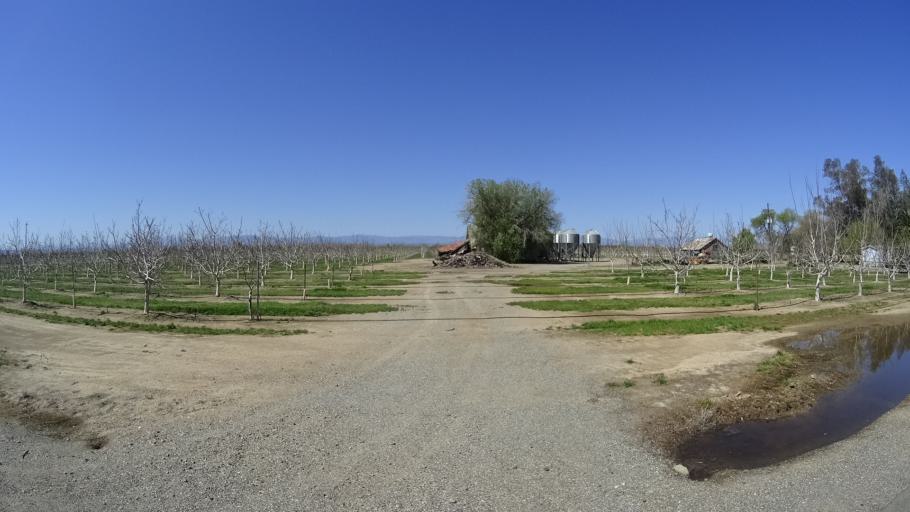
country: US
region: California
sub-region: Glenn County
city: Orland
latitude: 39.6765
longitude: -122.2343
